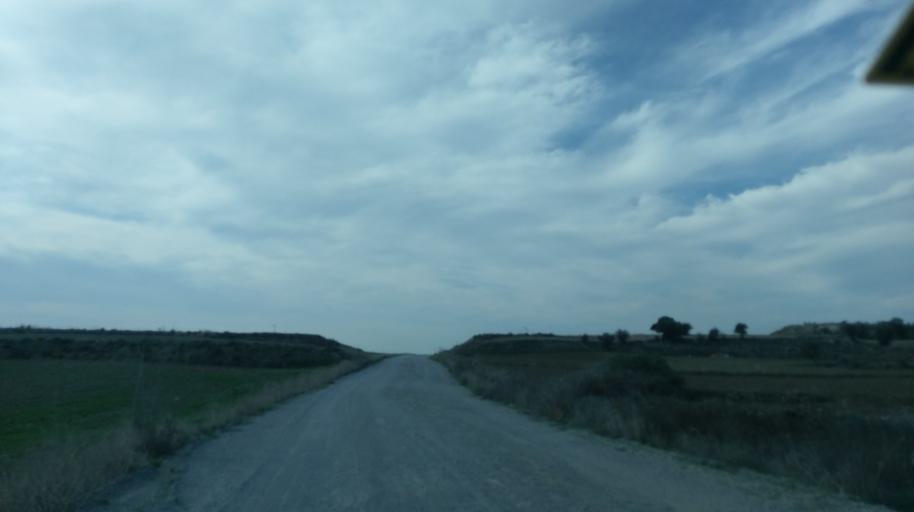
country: CY
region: Keryneia
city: Lapithos
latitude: 35.2885
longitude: 33.1329
